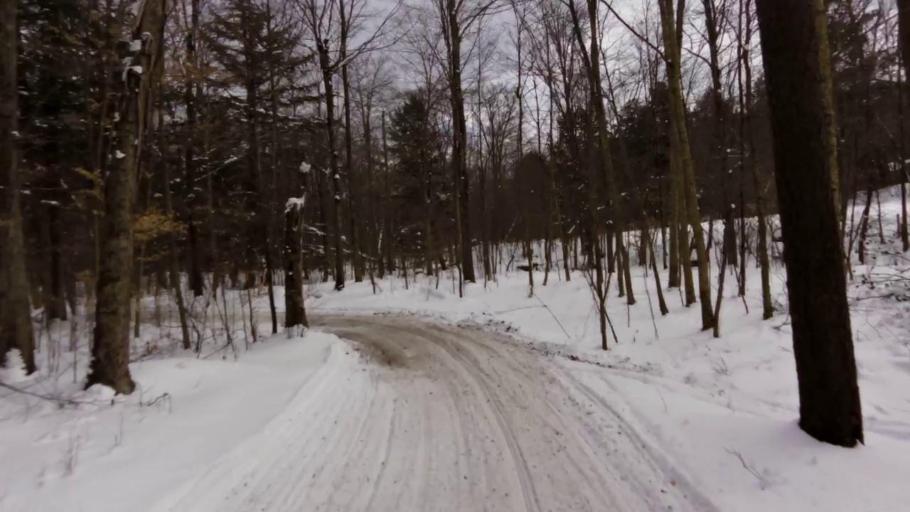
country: US
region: Pennsylvania
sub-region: McKean County
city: Bradford
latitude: 42.0115
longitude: -78.8070
